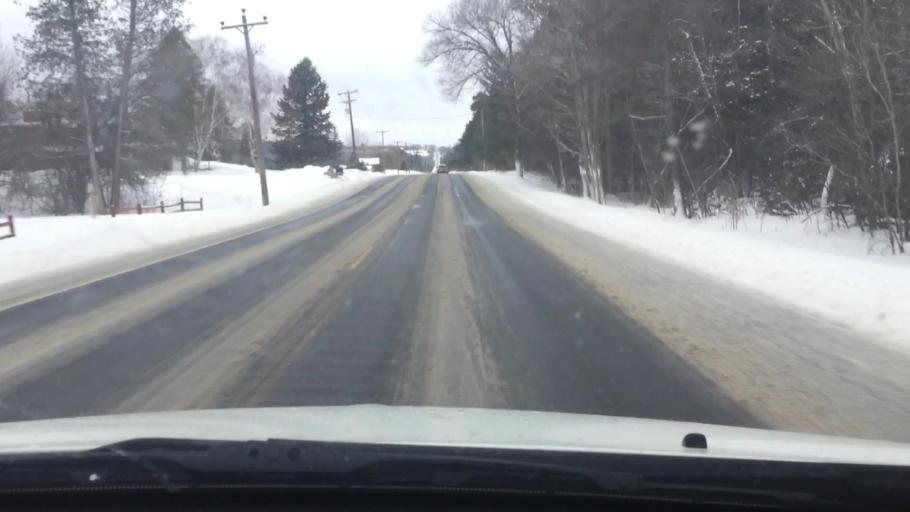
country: US
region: Michigan
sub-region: Charlevoix County
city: East Jordan
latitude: 45.1326
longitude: -85.1252
